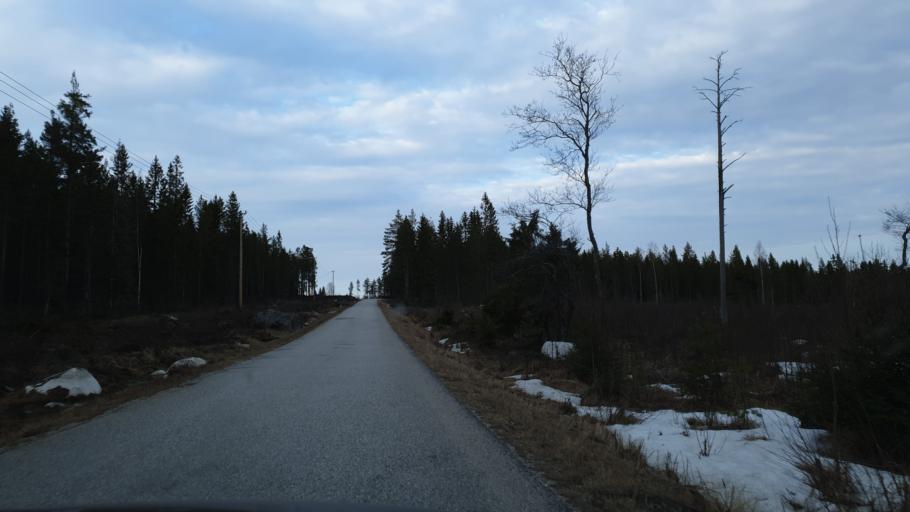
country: SE
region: Vaesternorrland
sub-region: Sundsvalls Kommun
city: Njurundabommen
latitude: 62.0096
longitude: 17.3963
